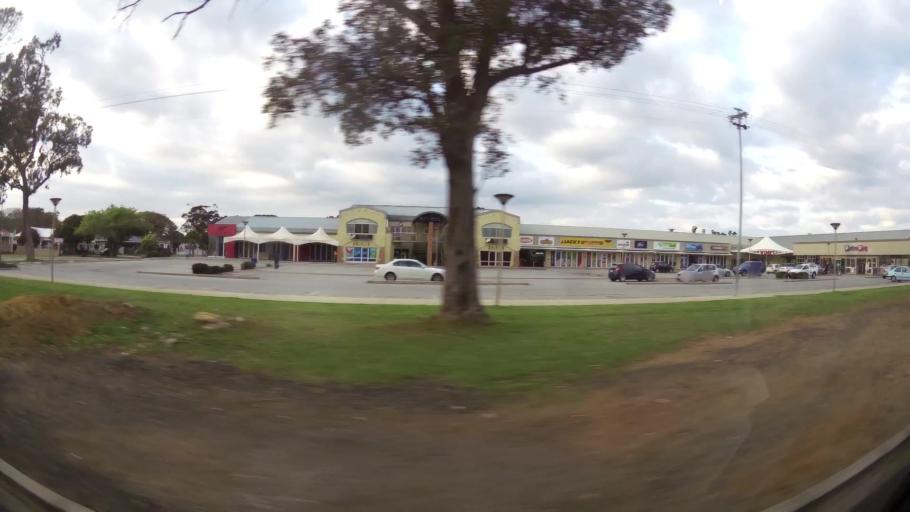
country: ZA
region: Eastern Cape
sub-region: Nelson Mandela Bay Metropolitan Municipality
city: Port Elizabeth
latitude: -33.9799
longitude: 25.5989
